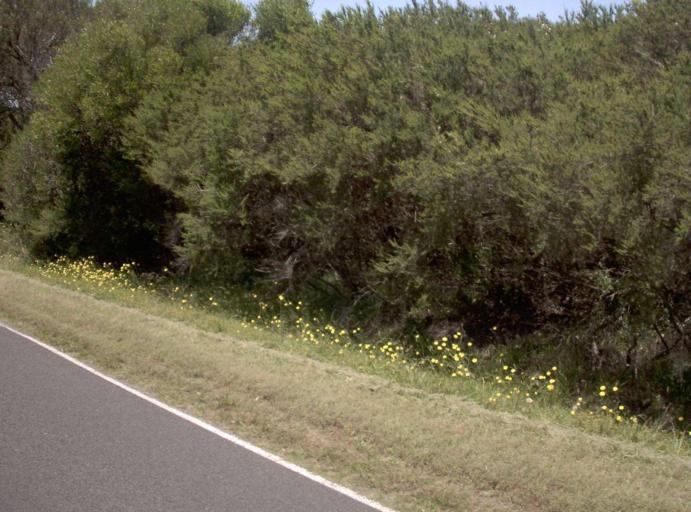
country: AU
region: Victoria
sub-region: Latrobe
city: Morwell
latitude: -38.7889
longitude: 146.1747
